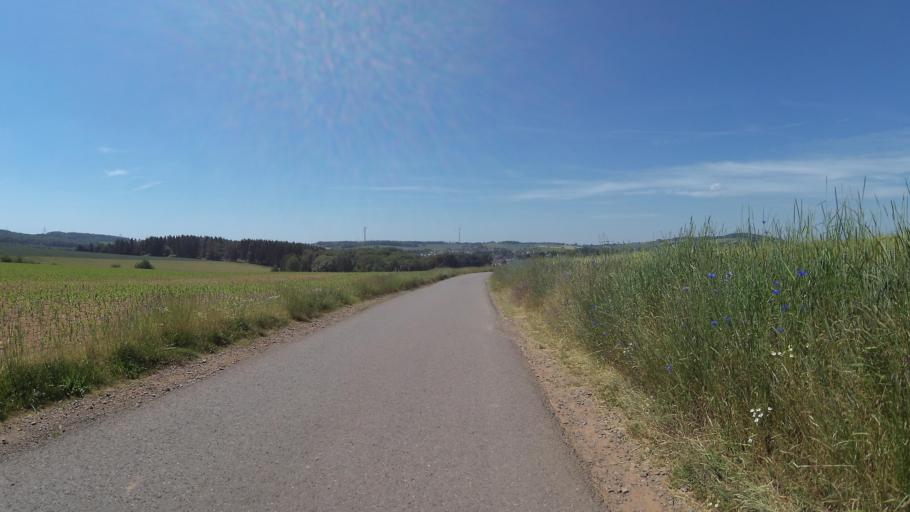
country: DE
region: Saarland
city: Eppelborn
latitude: 49.3979
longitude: 6.9387
